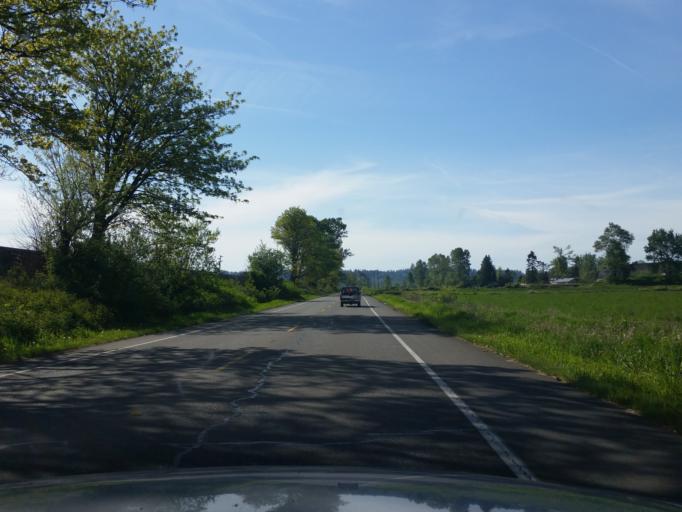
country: US
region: Washington
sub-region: Snohomish County
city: Fobes Hill
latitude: 47.9184
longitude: -122.1400
